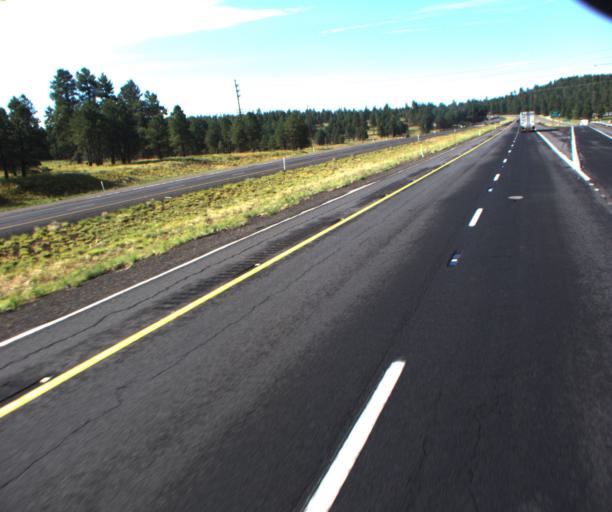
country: US
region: Arizona
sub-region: Coconino County
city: Kachina Village
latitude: 35.0938
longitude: -111.6849
